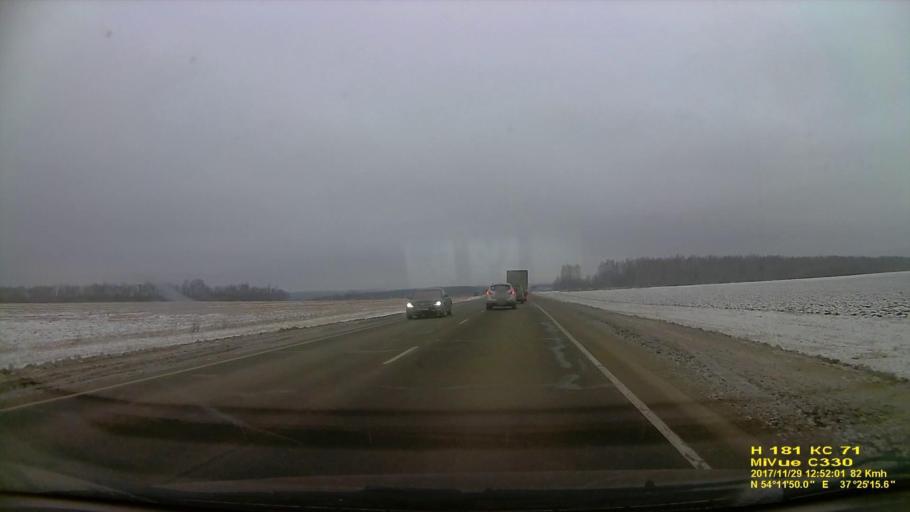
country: RU
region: Tula
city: Barsuki
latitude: 54.1974
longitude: 37.4207
